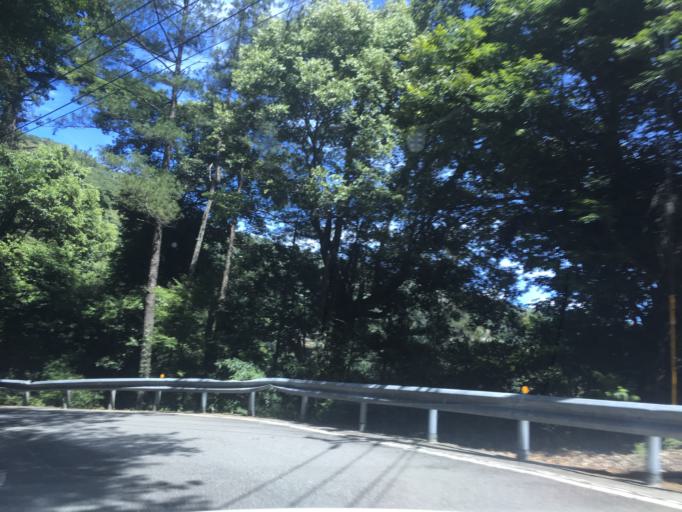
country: TW
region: Taiwan
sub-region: Nantou
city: Puli
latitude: 24.2216
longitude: 121.2638
